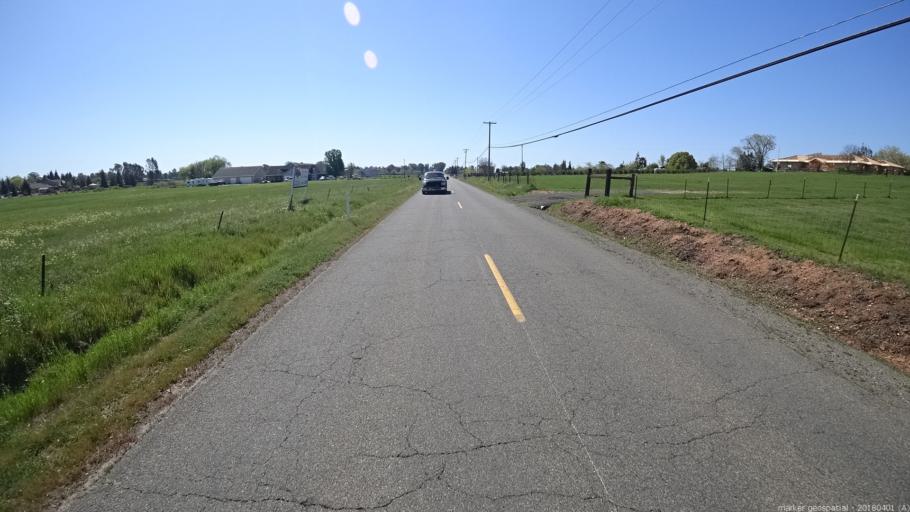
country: US
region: California
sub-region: Sacramento County
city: Wilton
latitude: 38.3934
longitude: -121.2422
